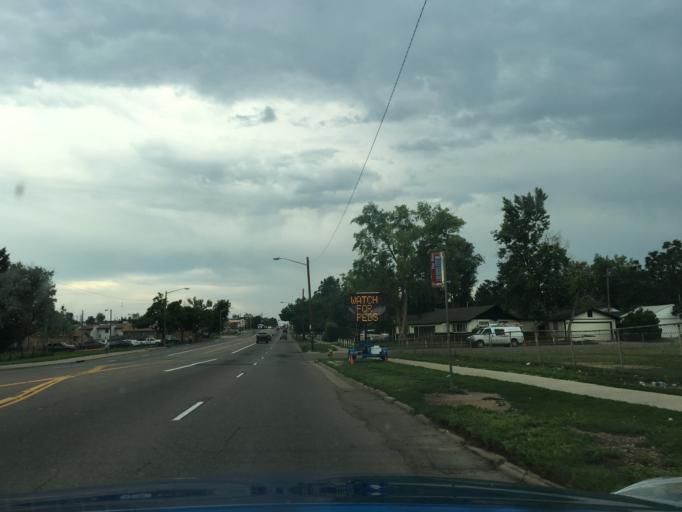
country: US
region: Colorado
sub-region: Arapahoe County
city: Sheridan
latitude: 39.6718
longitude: -105.0252
